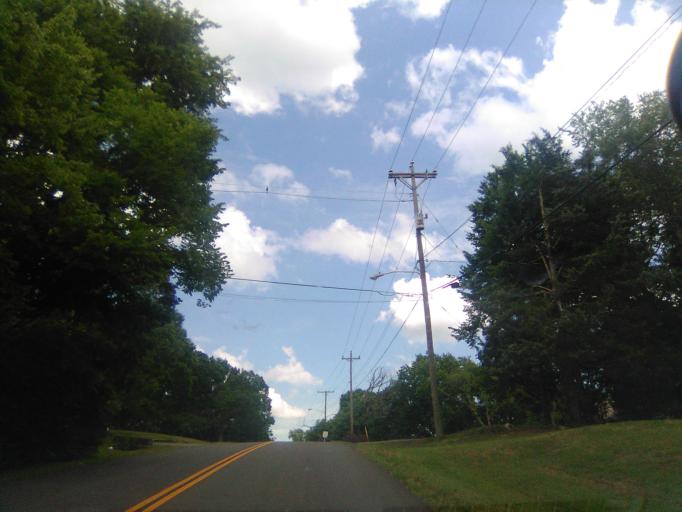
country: US
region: Tennessee
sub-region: Davidson County
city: Belle Meade
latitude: 36.1294
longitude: -86.8783
